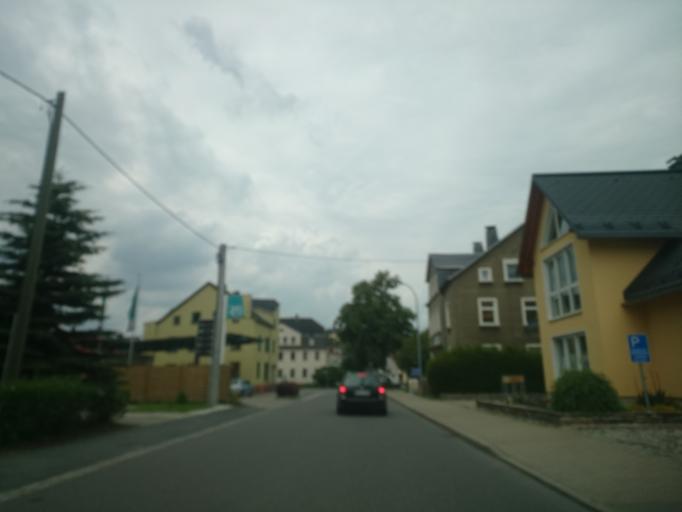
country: DE
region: Saxony
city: Eppendorf
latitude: 50.7960
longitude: 13.2288
